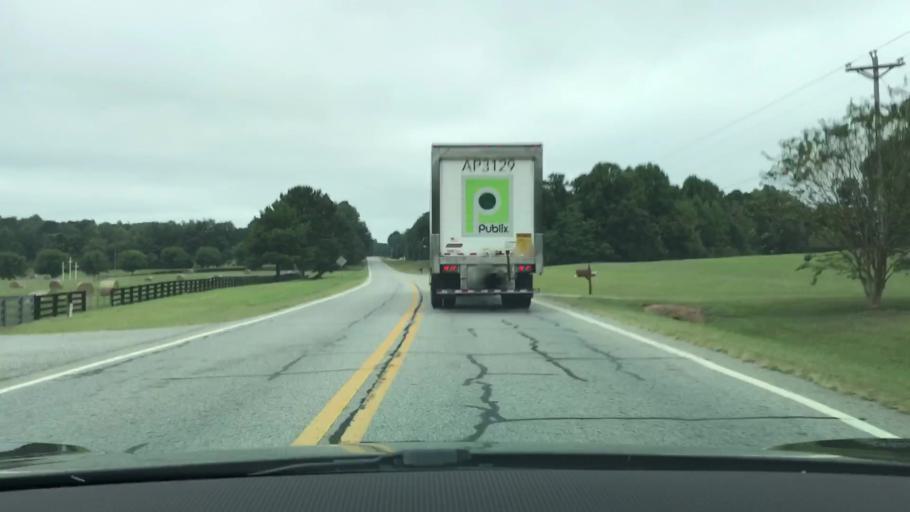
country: US
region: Georgia
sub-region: Oconee County
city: Watkinsville
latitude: 33.7518
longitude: -83.3022
